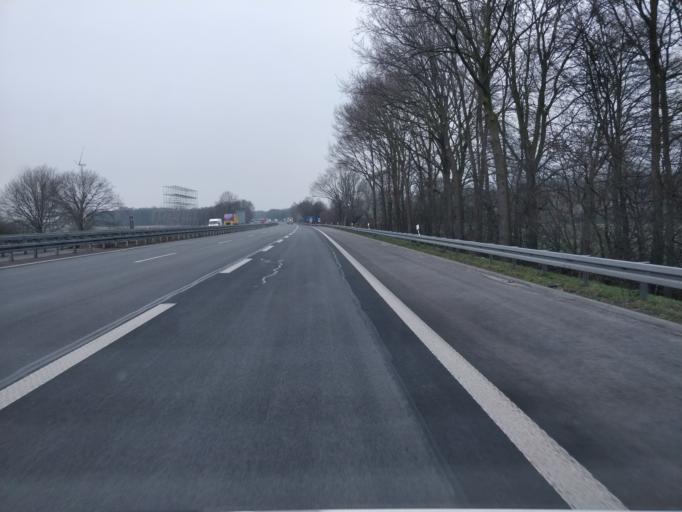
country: DE
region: North Rhine-Westphalia
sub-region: Regierungsbezirk Munster
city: Isselburg
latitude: 51.8185
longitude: 6.4371
